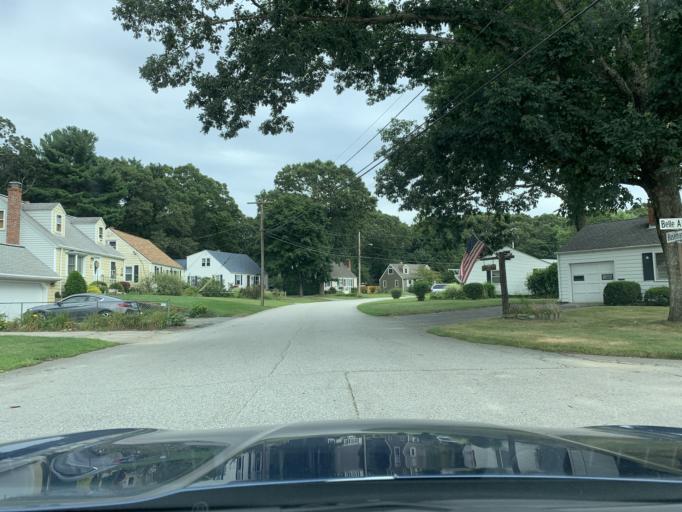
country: US
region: Rhode Island
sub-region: Kent County
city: East Greenwich
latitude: 41.6180
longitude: -71.4657
